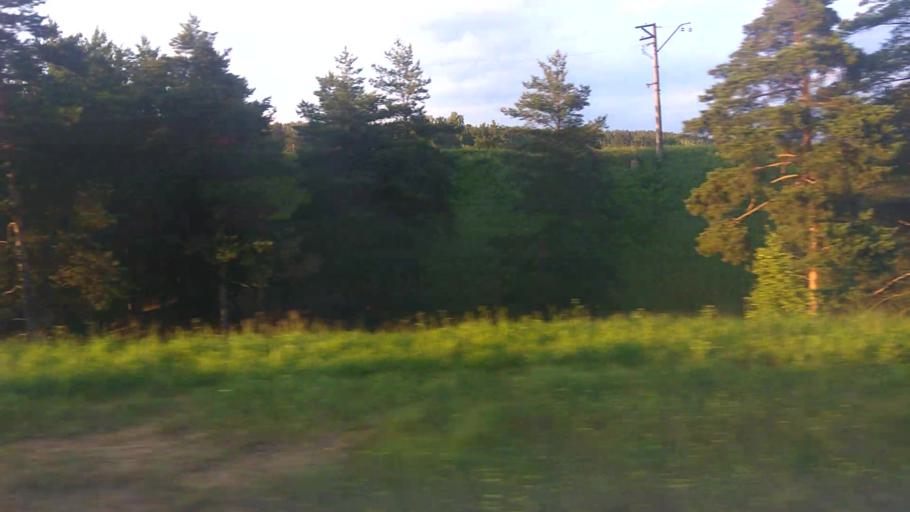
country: RU
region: Moskovskaya
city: Kashira
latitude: 54.8671
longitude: 38.1562
